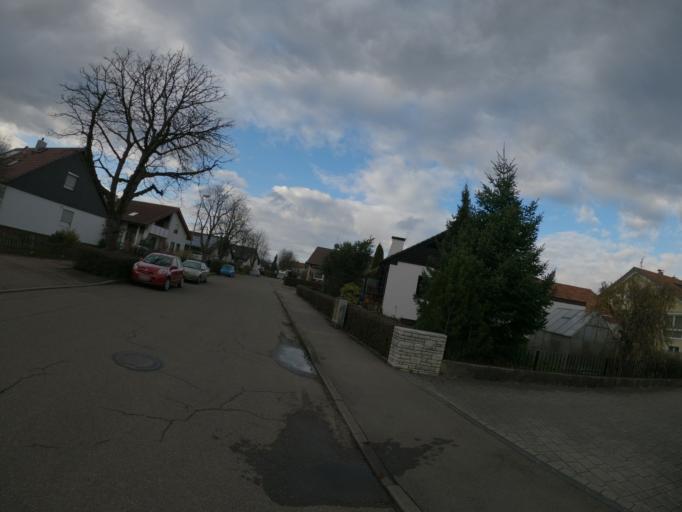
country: DE
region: Baden-Wuerttemberg
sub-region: Regierungsbezirk Stuttgart
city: Heiningen
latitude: 48.6595
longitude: 9.6396
